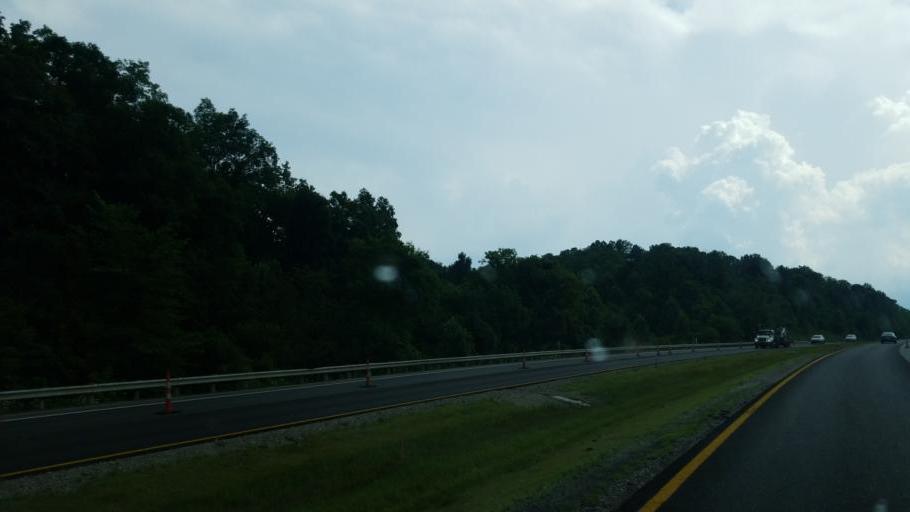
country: US
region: West Virginia
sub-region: Kanawha County
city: Alum Creek
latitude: 38.2469
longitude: -81.8370
